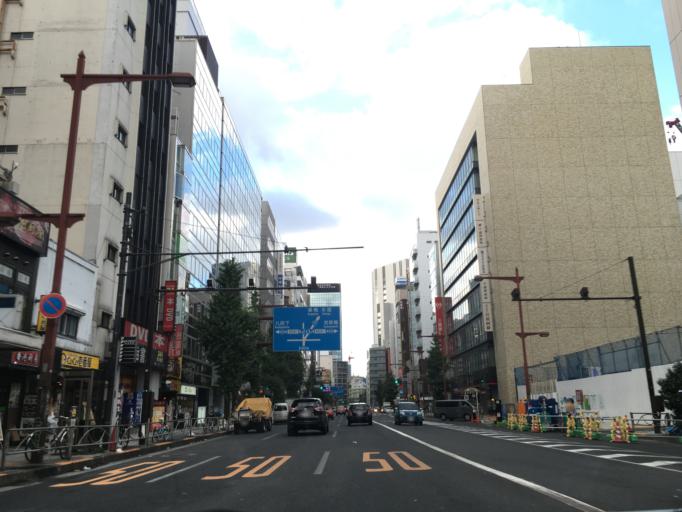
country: JP
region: Tokyo
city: Tokyo
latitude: 35.6936
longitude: 139.7709
